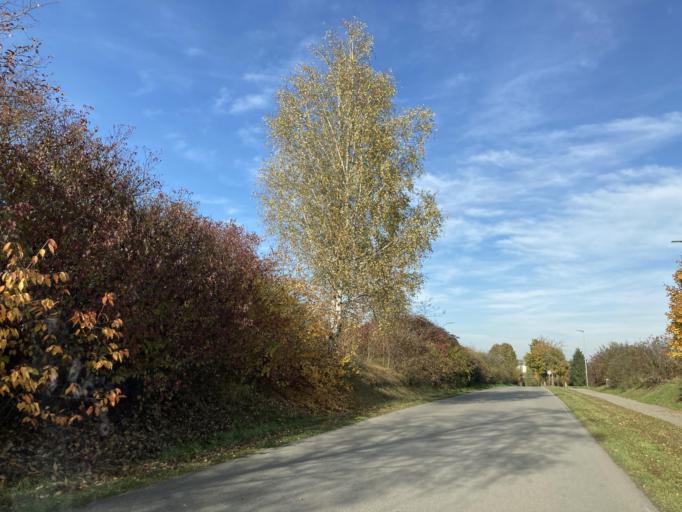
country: DE
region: Baden-Wuerttemberg
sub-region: Tuebingen Region
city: Rottenburg
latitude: 48.4585
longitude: 8.9403
